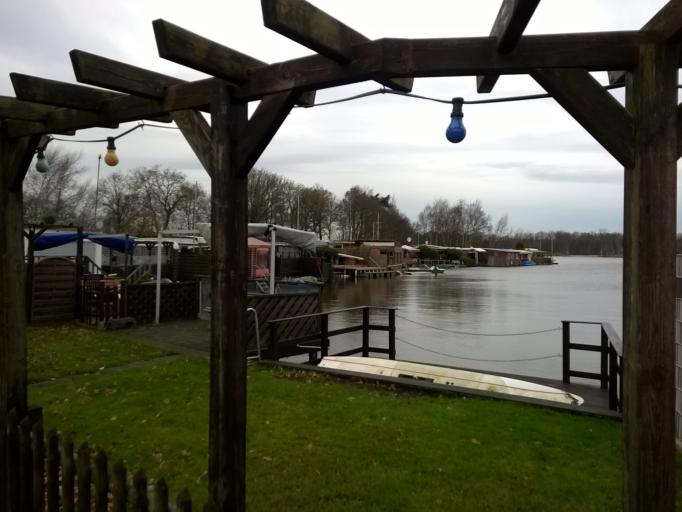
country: DE
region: Lower Saxony
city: Friedeburg
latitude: 53.4389
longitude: 7.8321
